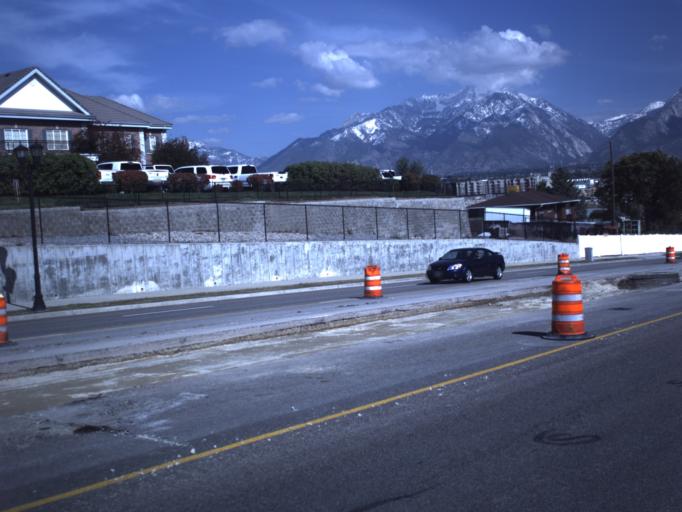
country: US
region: Utah
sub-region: Salt Lake County
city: South Jordan
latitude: 40.5593
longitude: -111.9154
